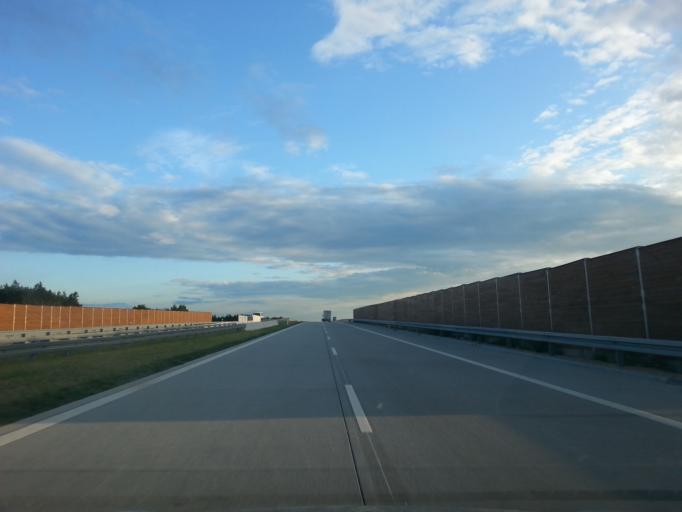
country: PL
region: Lodz Voivodeship
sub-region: Powiat sieradzki
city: Zloczew
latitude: 51.3775
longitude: 18.5470
